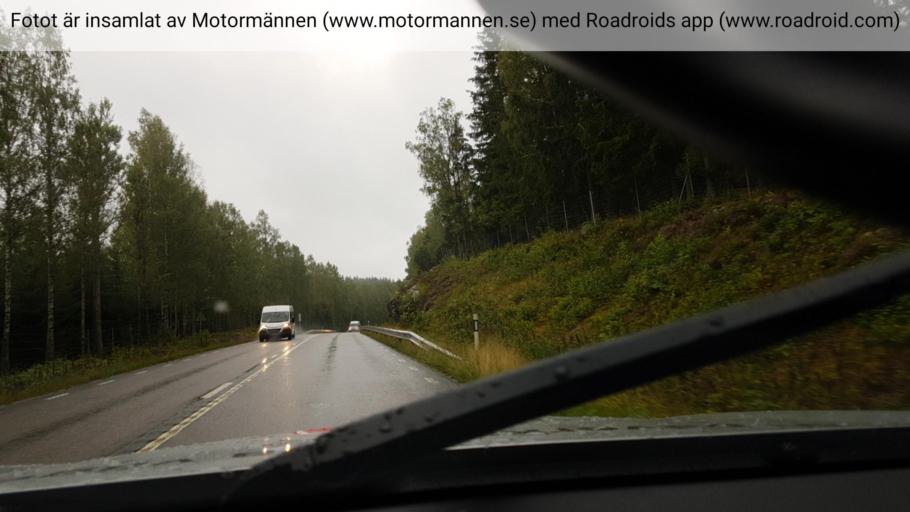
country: SE
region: Vaestra Goetaland
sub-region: Bengtsfors Kommun
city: Billingsfors
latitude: 59.0110
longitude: 12.2721
